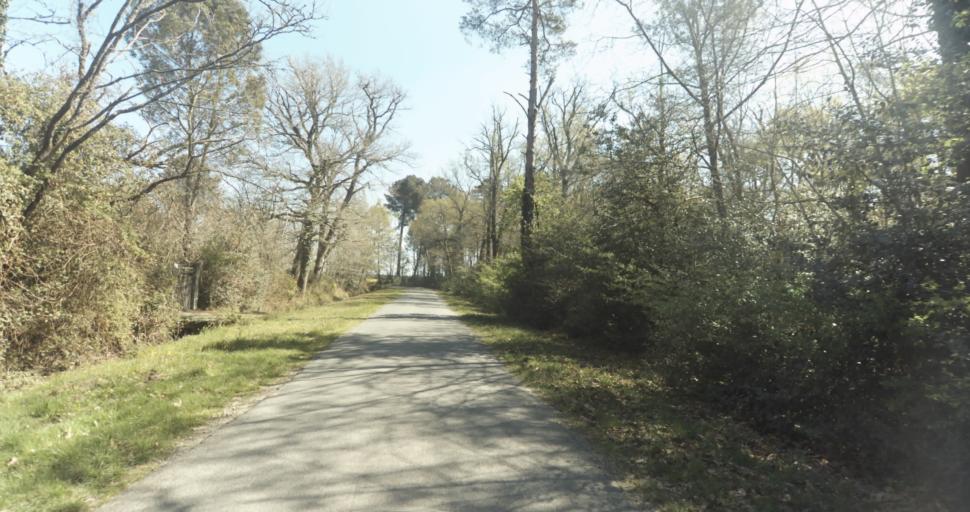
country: FR
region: Aquitaine
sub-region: Departement de la Gironde
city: Martignas-sur-Jalle
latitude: 44.7676
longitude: -0.8111
